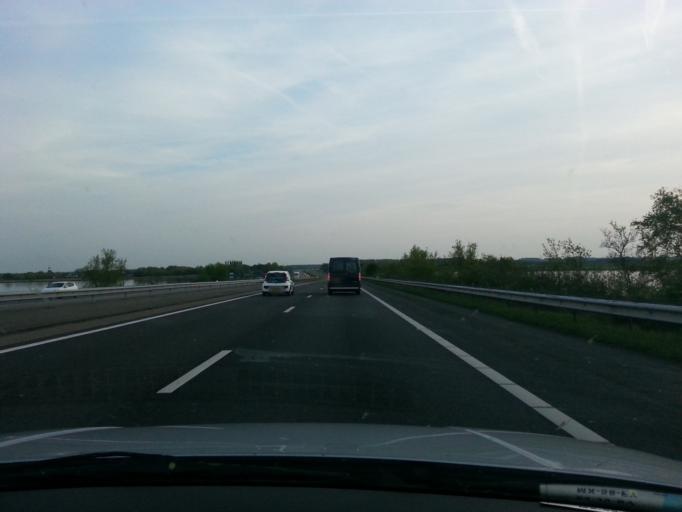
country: NL
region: Friesland
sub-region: Gemeente Skarsterlan
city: Sint Nicolaasga
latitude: 52.8848
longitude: 5.7553
